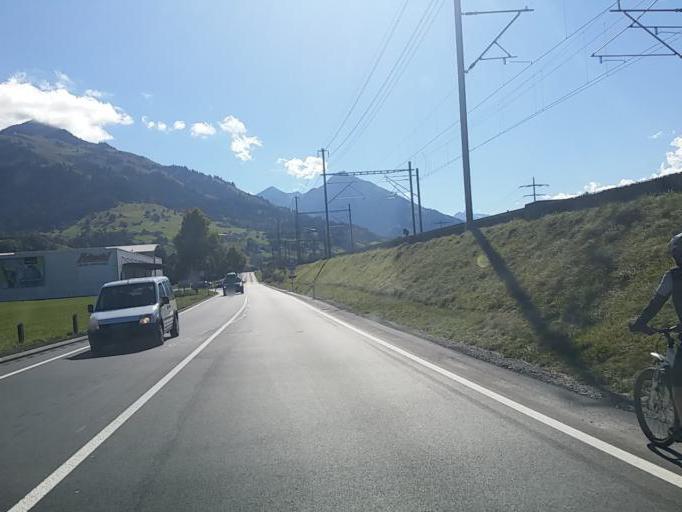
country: CH
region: Bern
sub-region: Frutigen-Niedersimmental District
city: Aeschi
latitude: 46.6294
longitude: 7.6914
